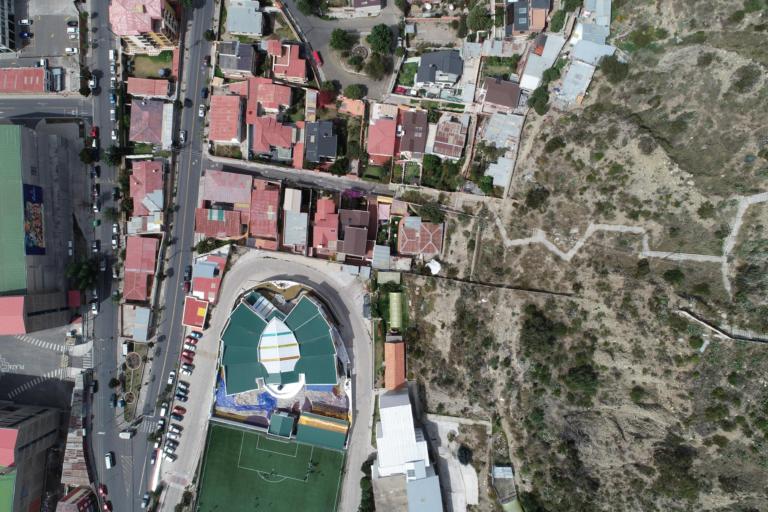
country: BO
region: La Paz
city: La Paz
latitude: -16.5382
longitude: -68.0975
